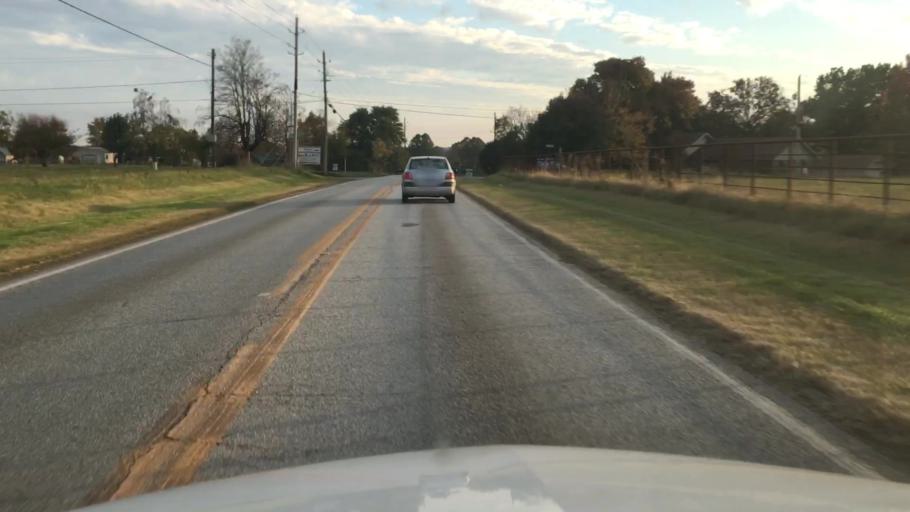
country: US
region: Arkansas
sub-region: Washington County
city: Elm Springs
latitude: 36.2205
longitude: -94.2304
